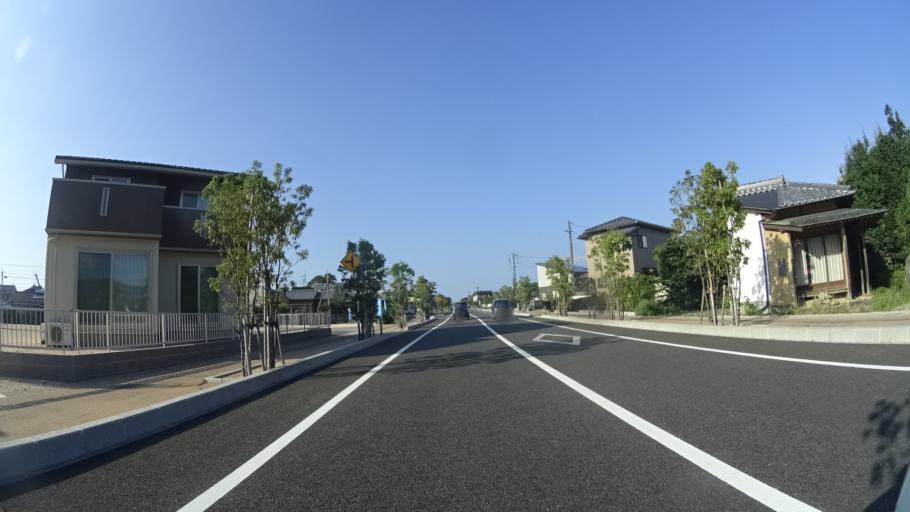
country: JP
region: Yamaguchi
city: Hagi
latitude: 34.4089
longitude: 131.3913
